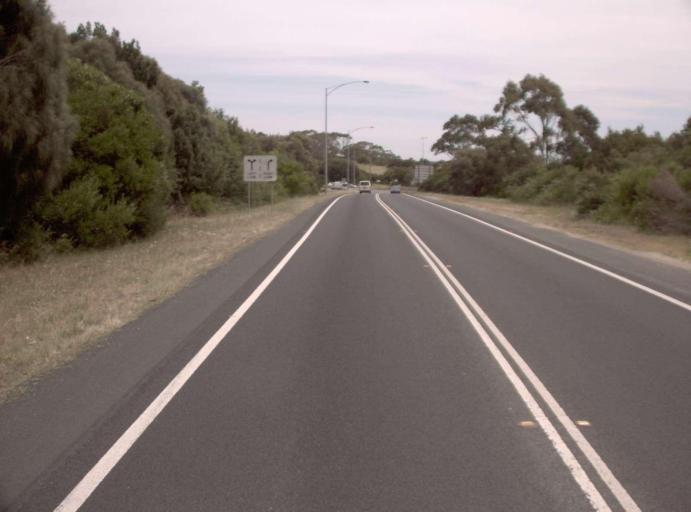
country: AU
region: Victoria
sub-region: Mornington Peninsula
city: Rosebud West
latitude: -38.3758
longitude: 144.8917
